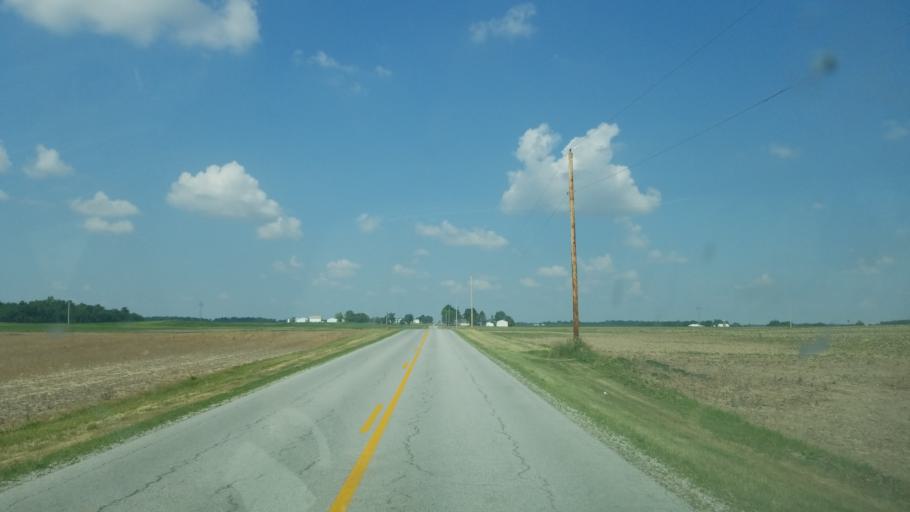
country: US
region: Ohio
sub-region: Auglaize County
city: Wapakoneta
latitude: 40.5707
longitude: -84.1046
